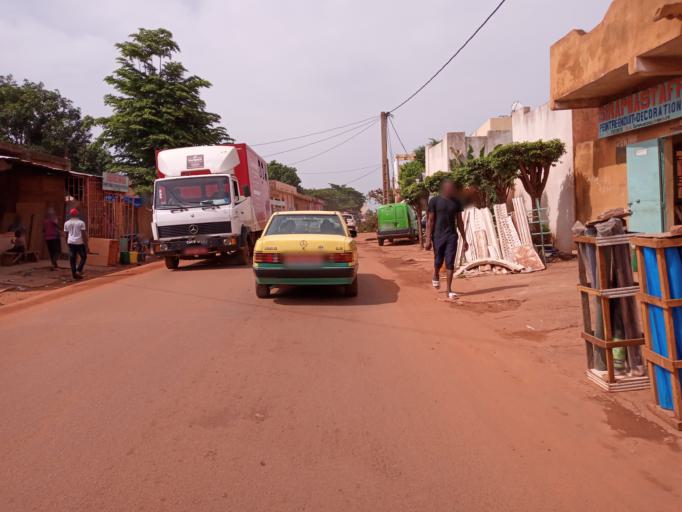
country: ML
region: Bamako
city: Bamako
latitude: 12.5666
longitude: -7.9898
